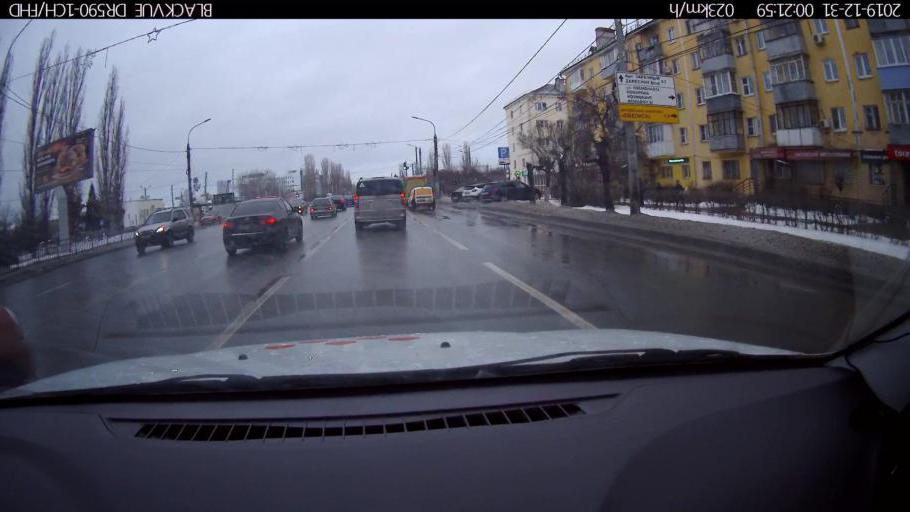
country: RU
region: Nizjnij Novgorod
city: Nizhniy Novgorod
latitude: 56.2833
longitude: 43.9265
